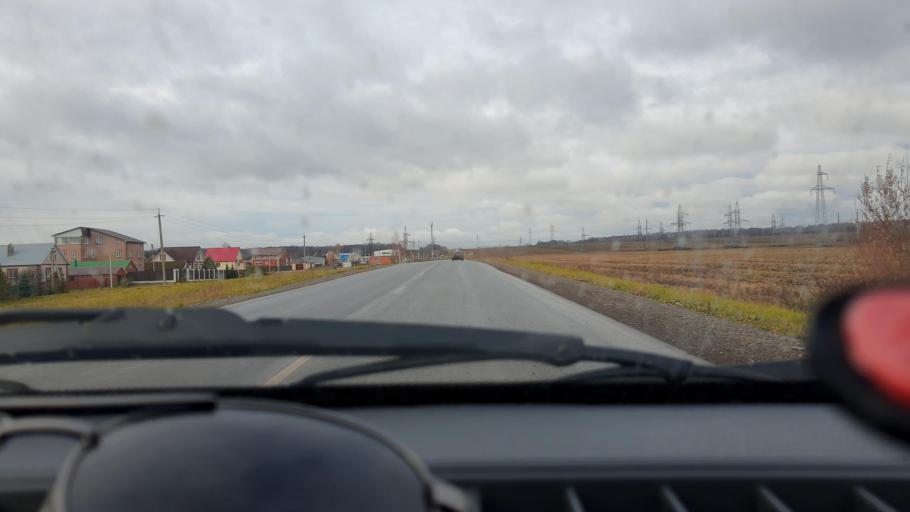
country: RU
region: Bashkortostan
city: Mikhaylovka
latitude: 54.8320
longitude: 55.9123
